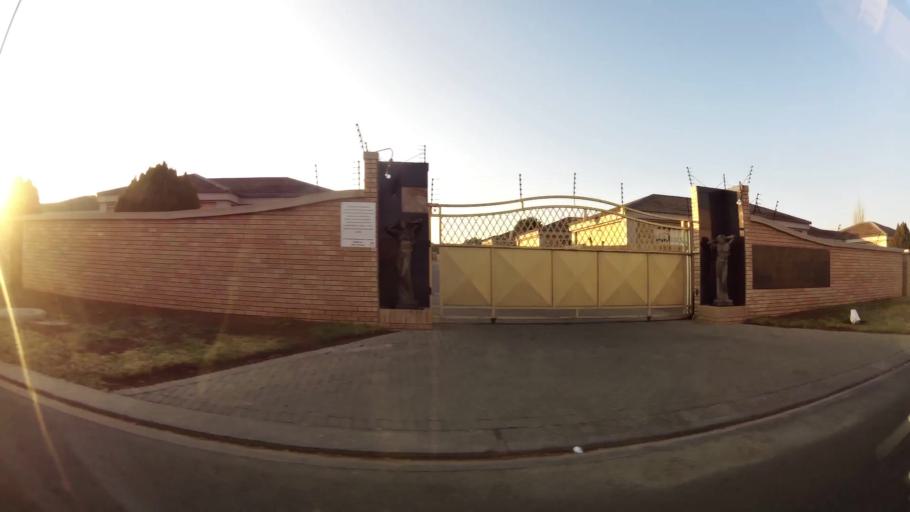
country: ZA
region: Orange Free State
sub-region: Mangaung Metropolitan Municipality
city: Bloemfontein
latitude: -29.0938
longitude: 26.1669
